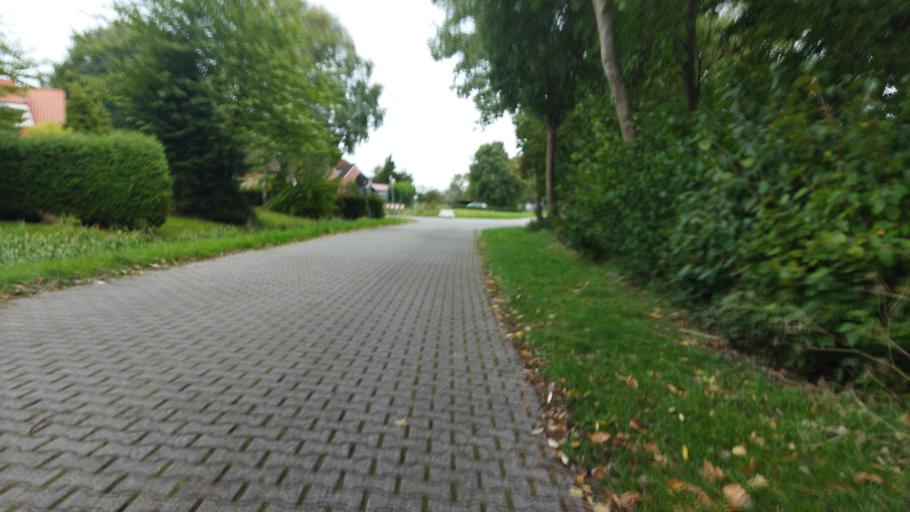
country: DE
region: Lower Saxony
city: Hinte
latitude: 53.4096
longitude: 7.1935
